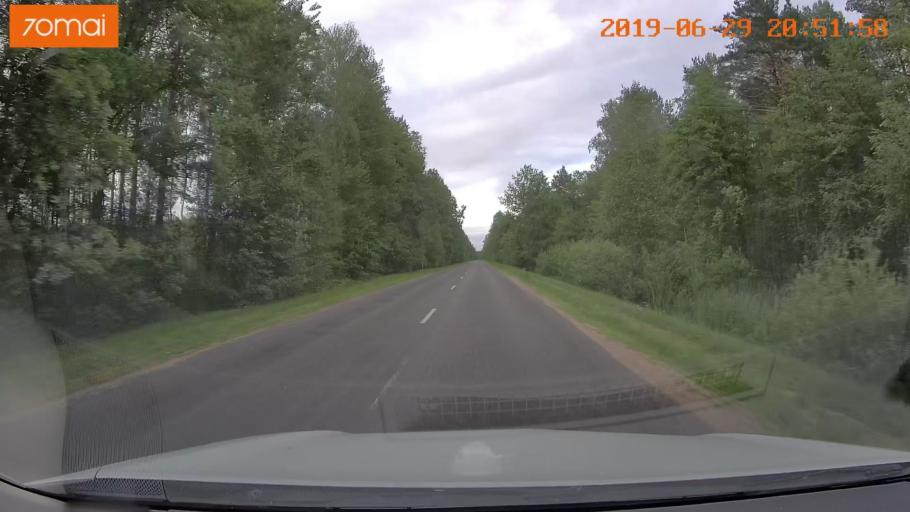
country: BY
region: Brest
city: Hantsavichy
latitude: 52.6942
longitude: 26.3567
